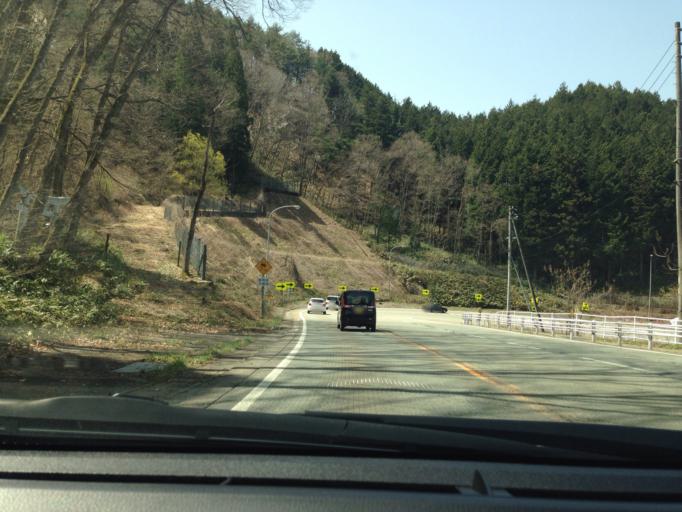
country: JP
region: Gifu
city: Takayama
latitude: 36.0808
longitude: 137.2563
